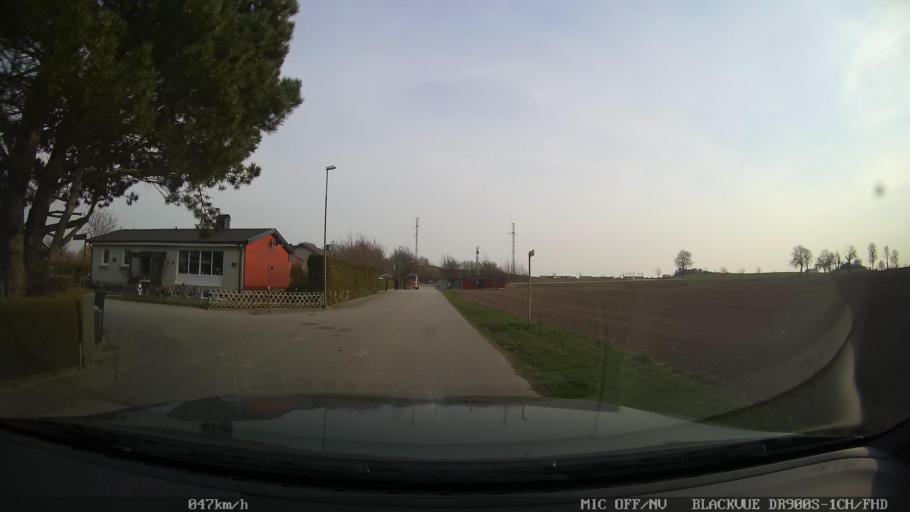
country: SE
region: Skane
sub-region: Ystads Kommun
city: Ystad
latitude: 55.4515
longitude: 13.7955
